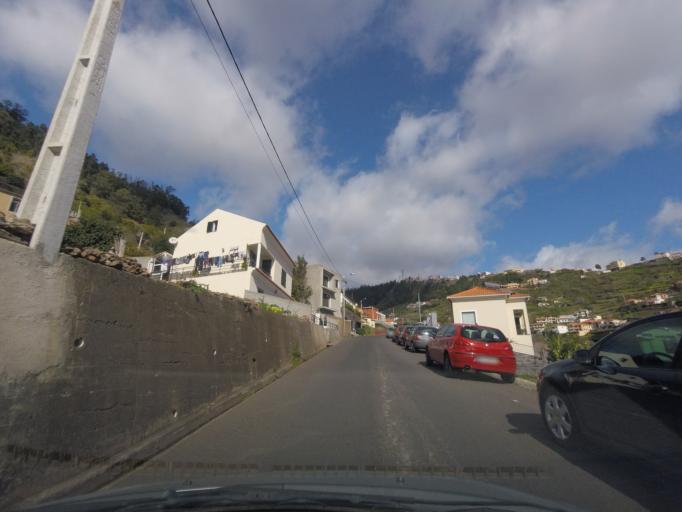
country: PT
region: Madeira
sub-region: Ribeira Brava
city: Campanario
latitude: 32.6619
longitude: -17.0106
